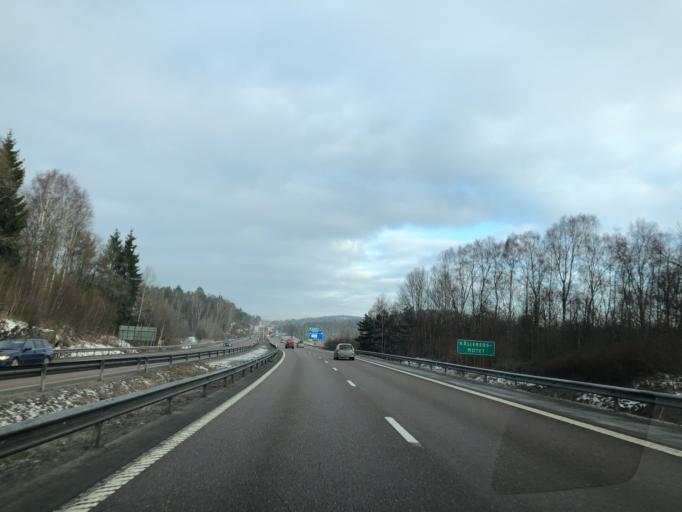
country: SE
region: Vaestra Goetaland
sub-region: Molndal
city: Kallered
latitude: 57.5900
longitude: 12.0634
